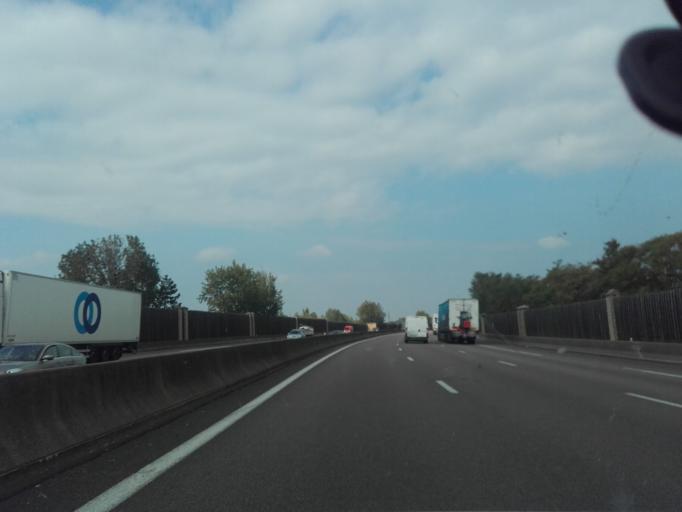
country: FR
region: Bourgogne
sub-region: Departement de Saone-et-Loire
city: Saint-Remy
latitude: 46.7731
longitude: 4.8196
